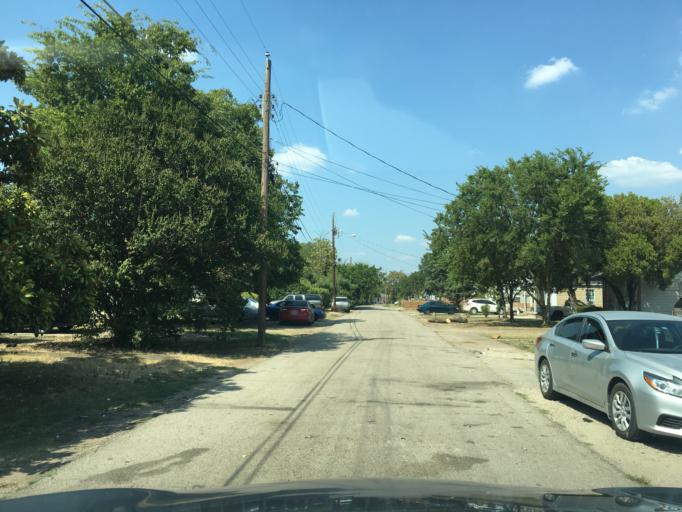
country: US
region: Texas
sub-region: Dallas County
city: Dallas
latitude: 32.7377
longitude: -96.7950
